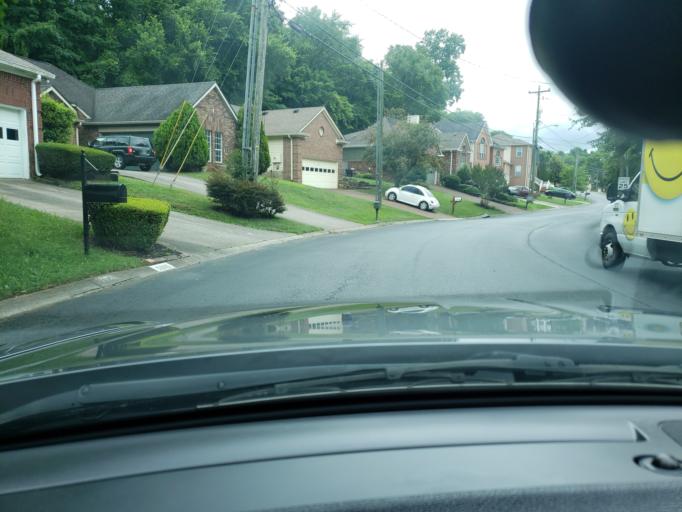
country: US
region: Tennessee
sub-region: Williamson County
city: Nolensville
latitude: 36.0350
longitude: -86.6763
